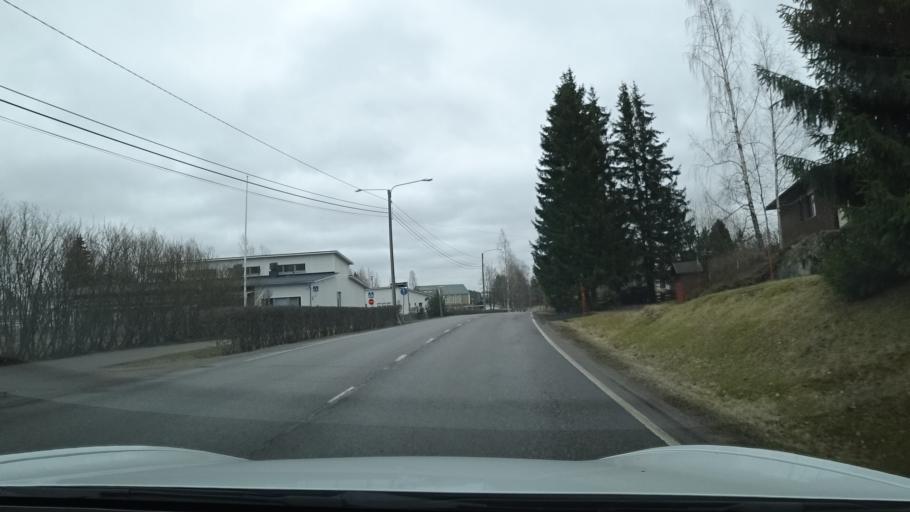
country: FI
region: Uusimaa
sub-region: Porvoo
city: Askola
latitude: 60.4975
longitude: 25.5313
